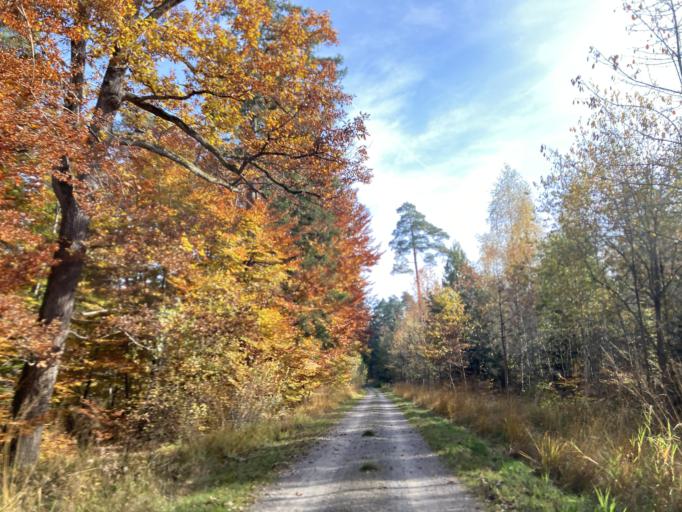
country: DE
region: Baden-Wuerttemberg
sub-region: Tuebingen Region
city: Bodelshausen
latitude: 48.4173
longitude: 8.9508
